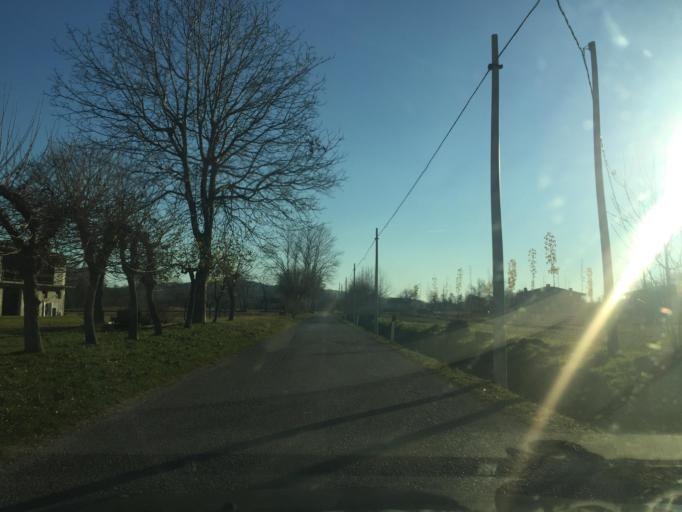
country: IT
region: Friuli Venezia Giulia
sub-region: Provincia di Udine
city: Osoppo
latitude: 46.2490
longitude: 13.1098
